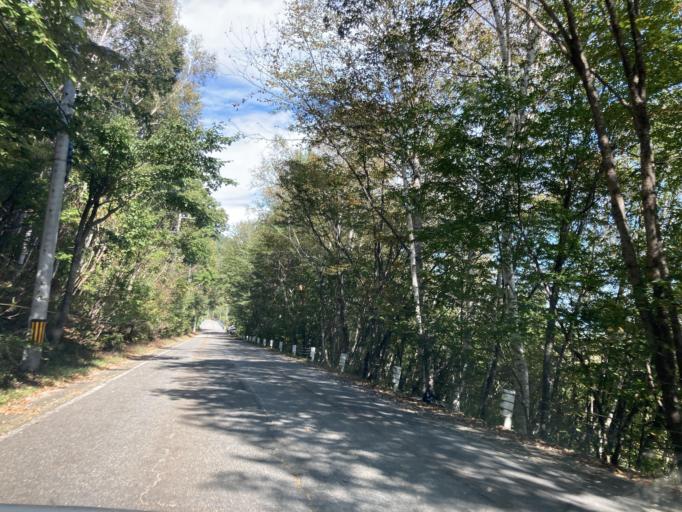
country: JP
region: Nagano
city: Omachi
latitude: 36.5173
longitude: 137.7797
